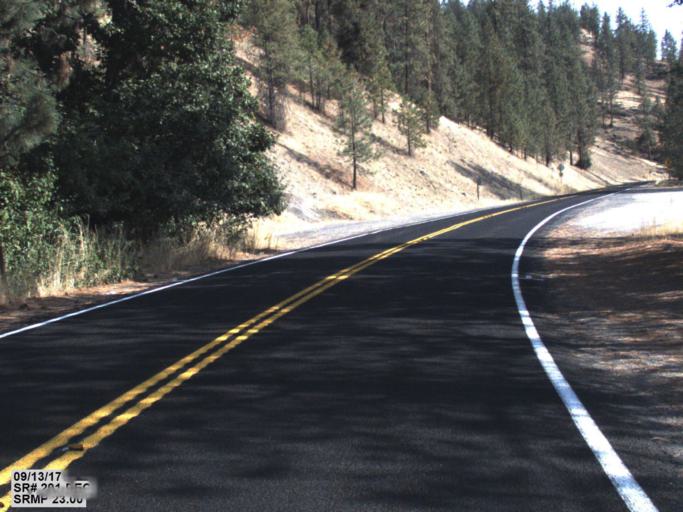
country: US
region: Washington
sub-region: Spokane County
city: Deer Park
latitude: 47.8846
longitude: -117.6976
